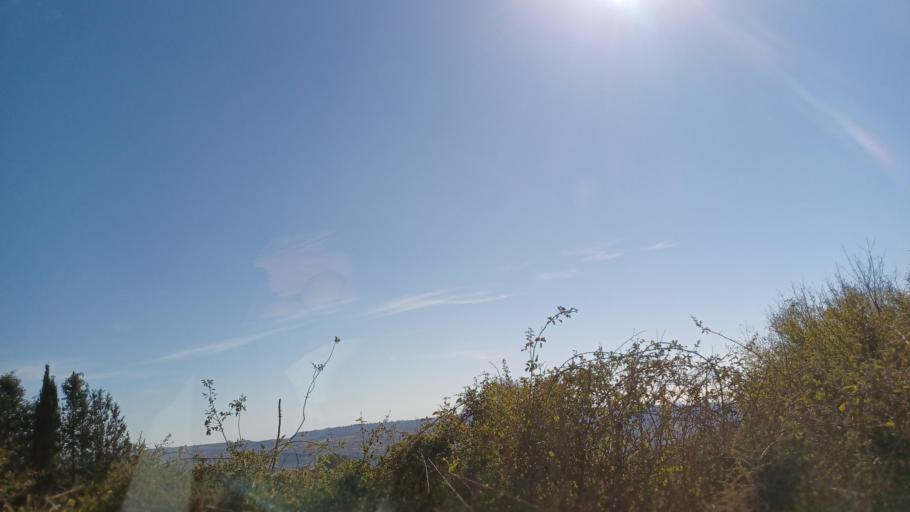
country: CY
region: Pafos
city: Pegeia
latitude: 34.9547
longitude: 32.3907
